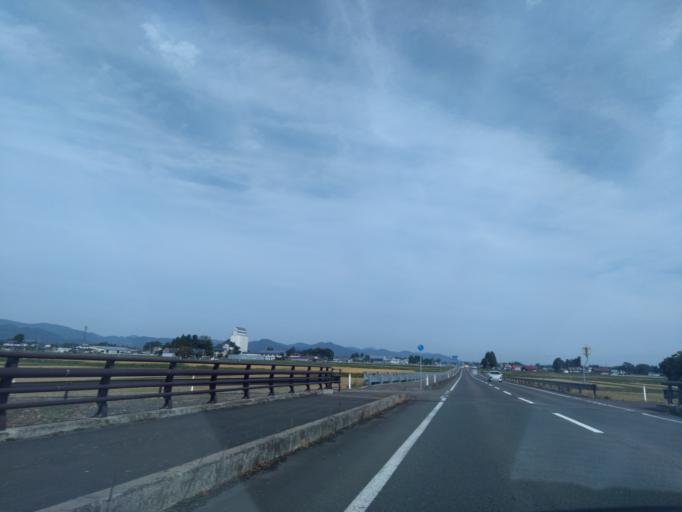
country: JP
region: Iwate
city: Hanamaki
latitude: 39.3527
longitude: 141.0553
